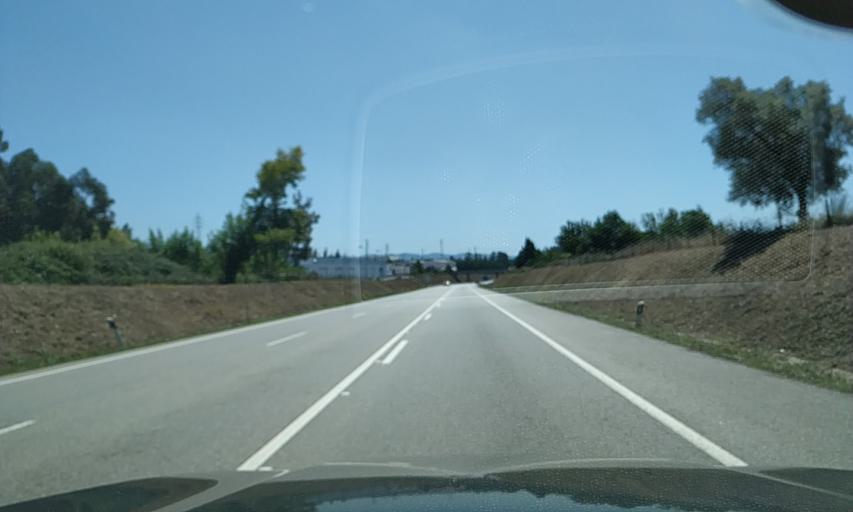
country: PT
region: Aveiro
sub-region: Oliveira do Bairro
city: Oliveira do Bairro
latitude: 40.5388
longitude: -8.4631
